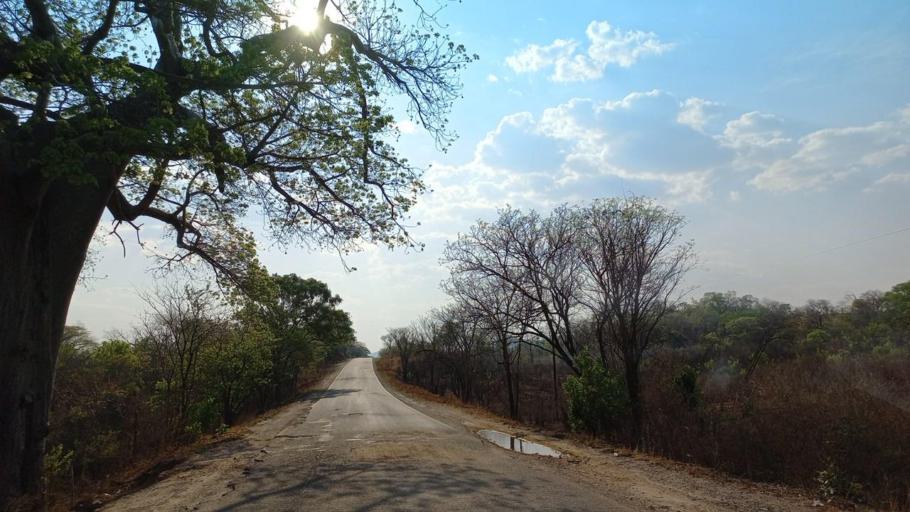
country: ZM
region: Lusaka
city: Luangwa
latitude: -14.9821
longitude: 30.1383
